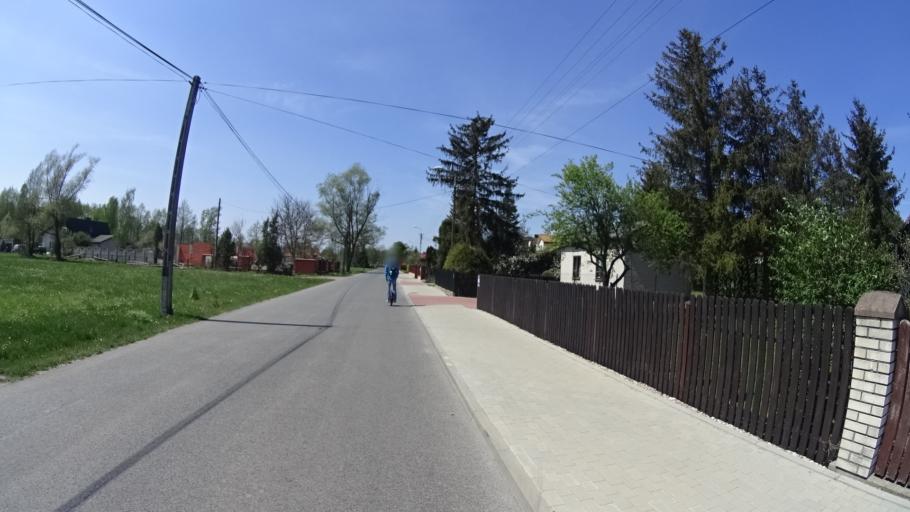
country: PL
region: Masovian Voivodeship
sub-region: Powiat warszawski zachodni
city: Truskaw
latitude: 52.2835
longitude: 20.7337
